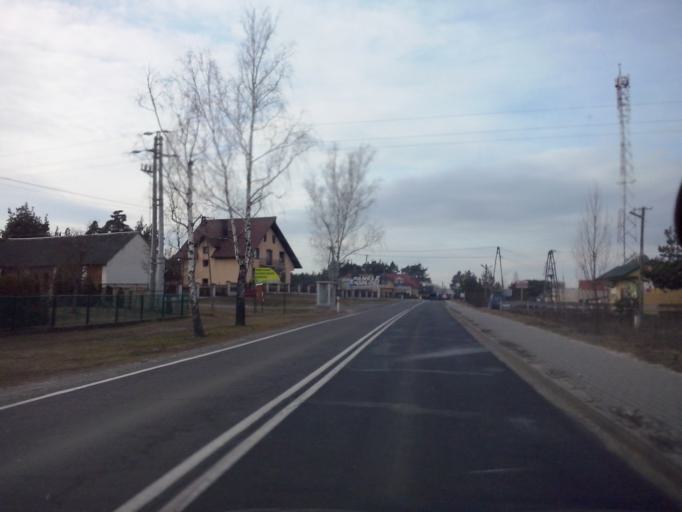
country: PL
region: Lublin Voivodeship
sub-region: Powiat bilgorajski
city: Biszcza
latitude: 50.4933
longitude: 22.6329
